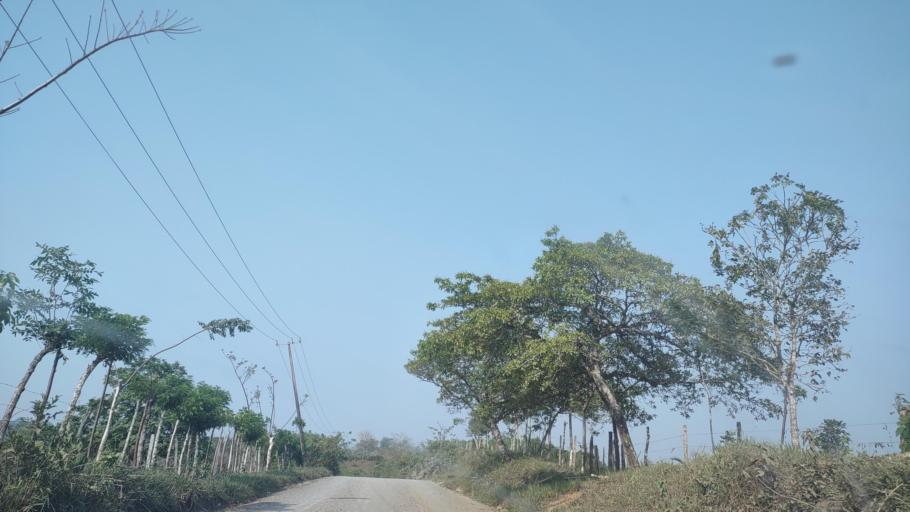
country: MX
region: Tabasco
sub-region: Huimanguillo
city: Francisco Rueda
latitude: 17.6430
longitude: -93.9114
